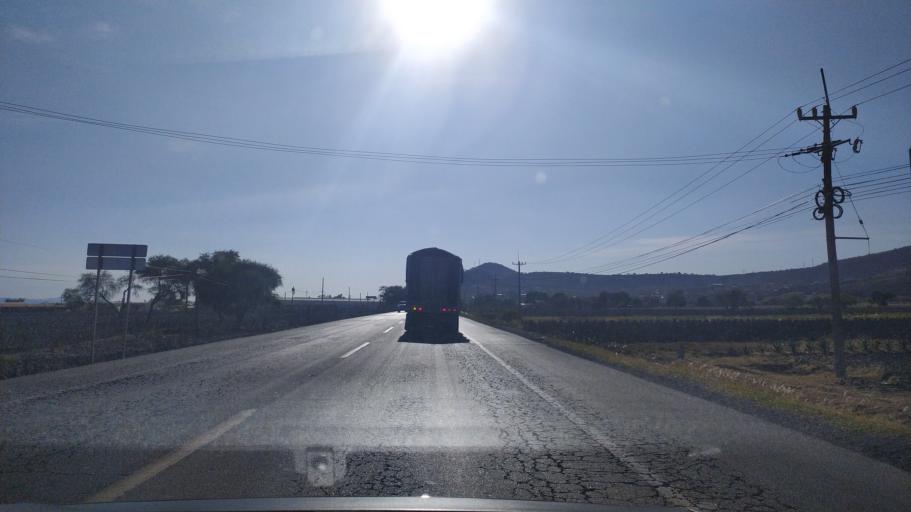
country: MX
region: Jalisco
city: Jamay
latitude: 20.2945
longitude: -102.6901
